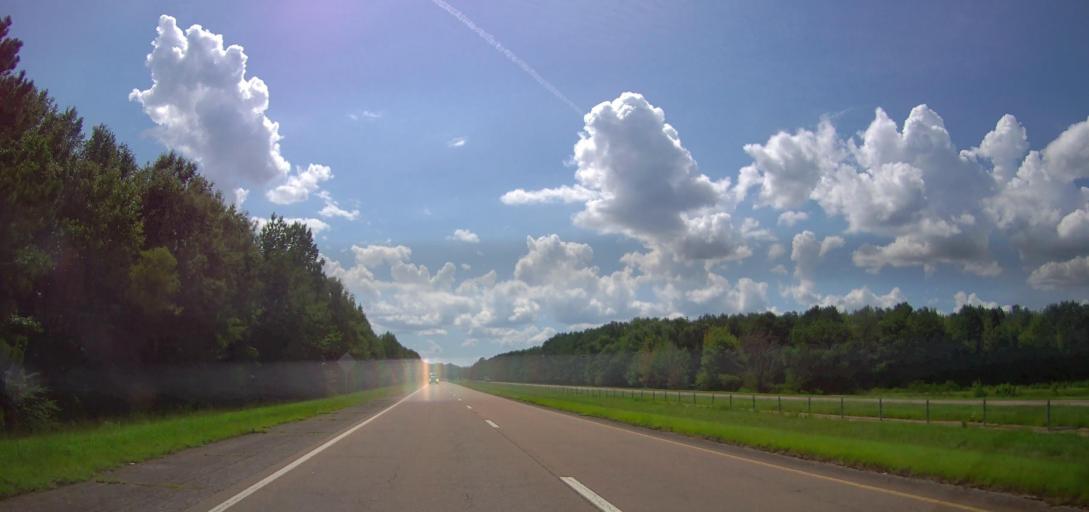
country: US
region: Mississippi
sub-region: Lowndes County
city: New Hope
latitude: 33.5086
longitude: -88.3448
